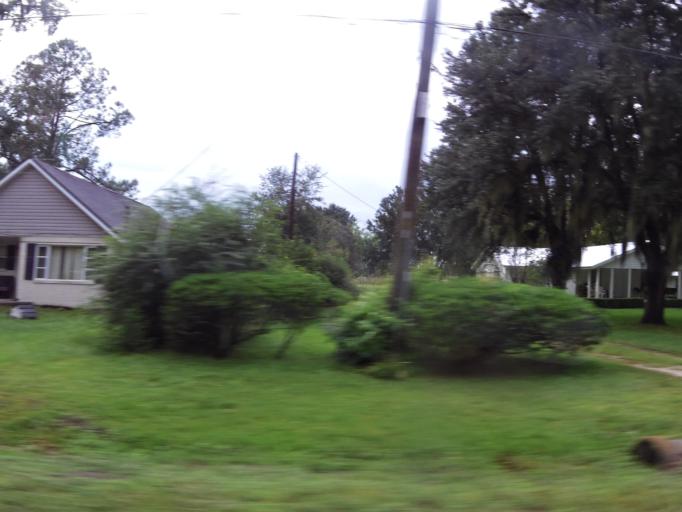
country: US
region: Florida
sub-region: Duval County
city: Baldwin
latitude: 30.3176
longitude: -81.8946
